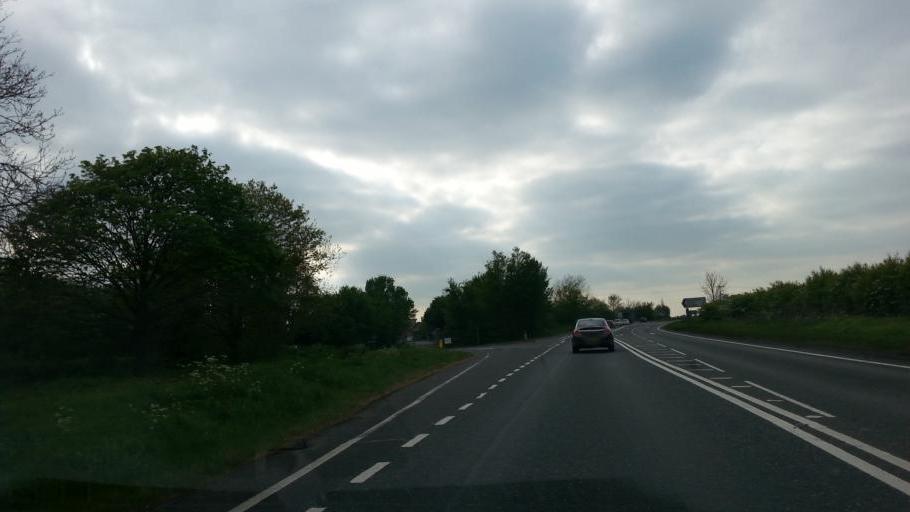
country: GB
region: England
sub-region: Nottinghamshire
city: South Collingham
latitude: 53.0722
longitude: -0.6845
